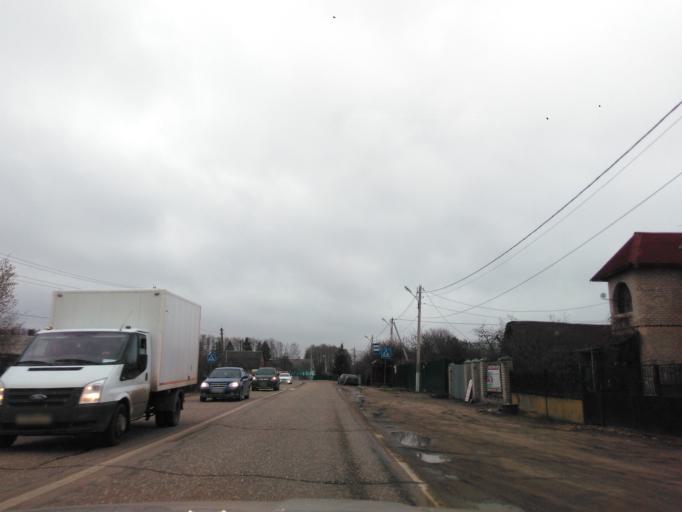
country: RU
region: Moskovskaya
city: Nakhabino
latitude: 55.8303
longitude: 37.1487
